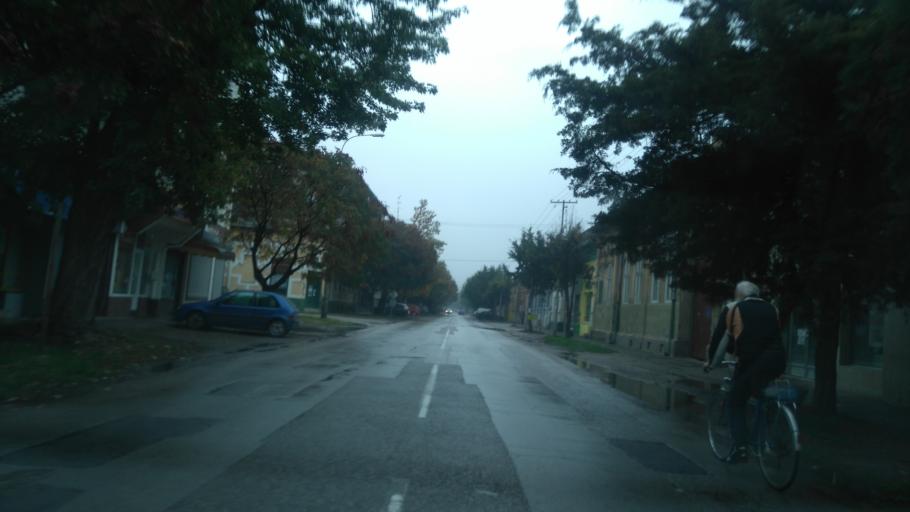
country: RS
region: Autonomna Pokrajina Vojvodina
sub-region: Juznobacki Okrug
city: Becej
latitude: 45.6193
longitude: 20.0424
